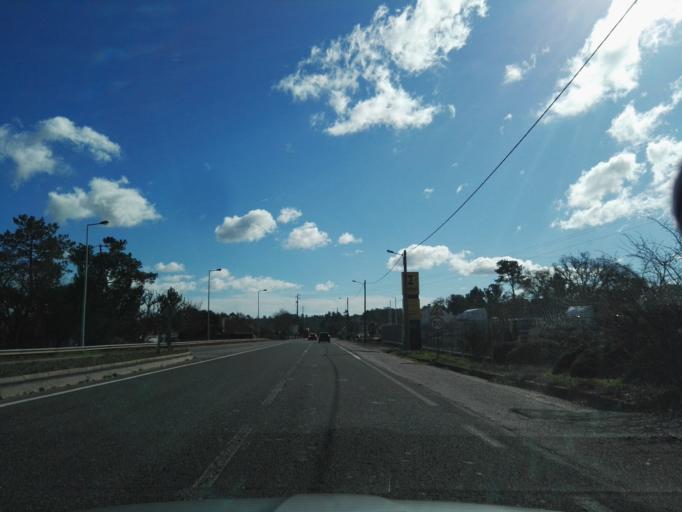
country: PT
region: Santarem
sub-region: Ourem
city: Fatima
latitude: 39.6287
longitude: -8.6813
